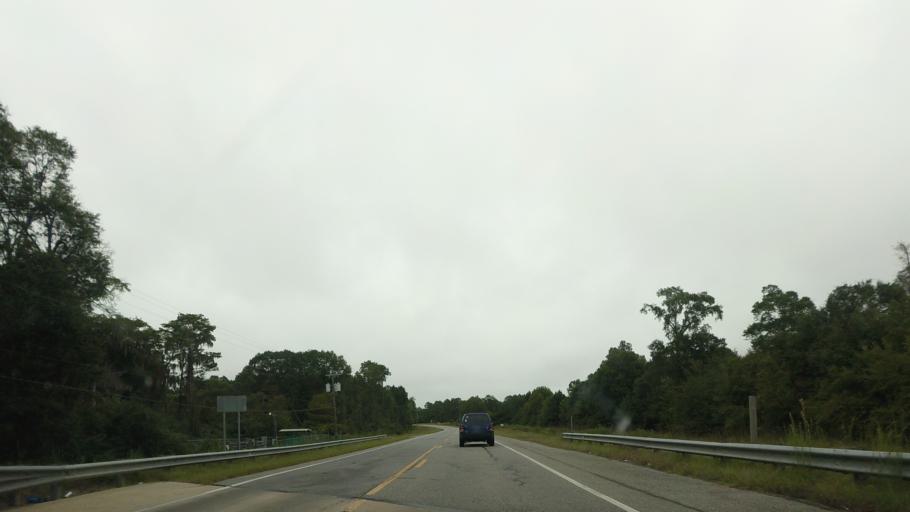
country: US
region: Georgia
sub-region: Irwin County
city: Ocilla
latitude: 31.5805
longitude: -83.2518
